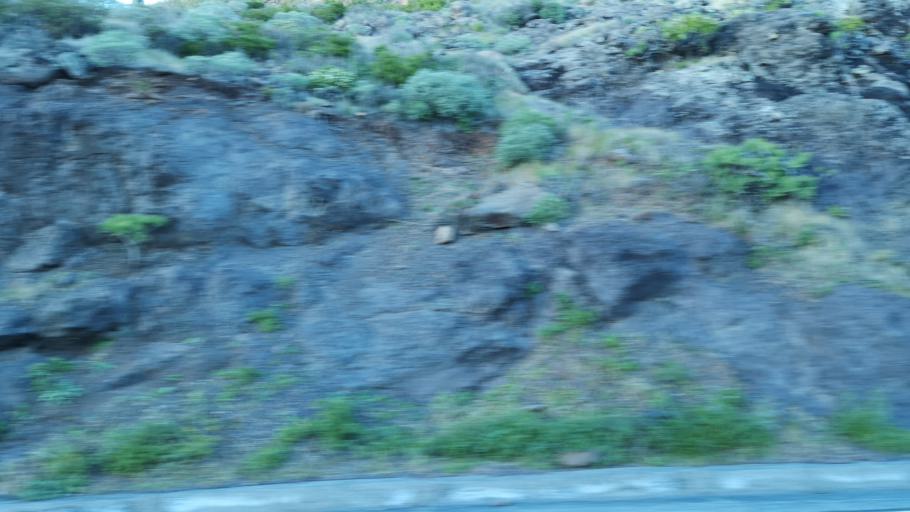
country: ES
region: Canary Islands
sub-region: Provincia de Santa Cruz de Tenerife
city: Alajero
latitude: 28.0852
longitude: -17.2459
